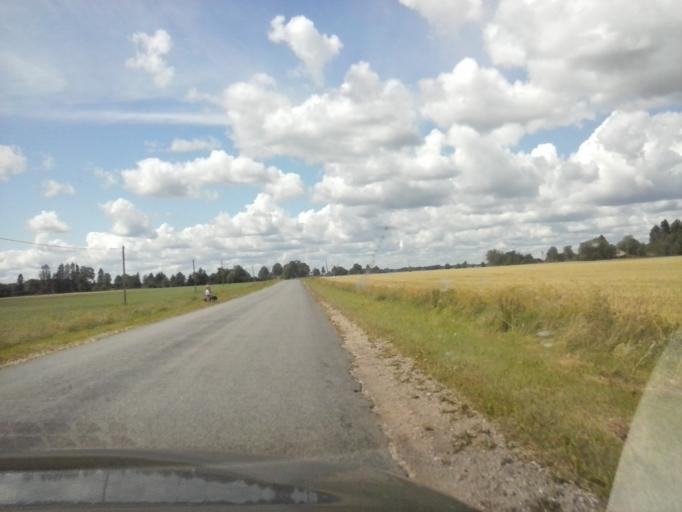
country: EE
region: Laeaene-Virumaa
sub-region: Rakke vald
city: Rakke
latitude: 59.0539
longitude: 26.3546
